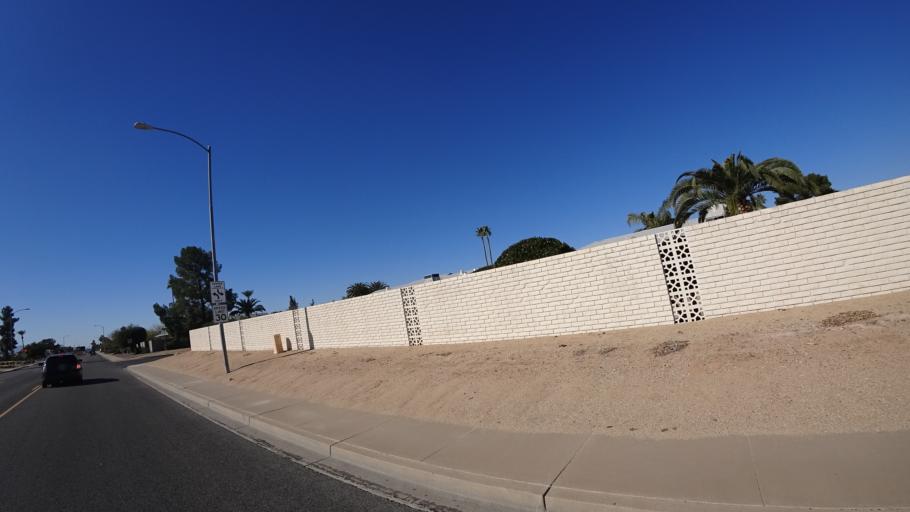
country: US
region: Arizona
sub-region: Maricopa County
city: Surprise
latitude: 33.6525
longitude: -112.2840
